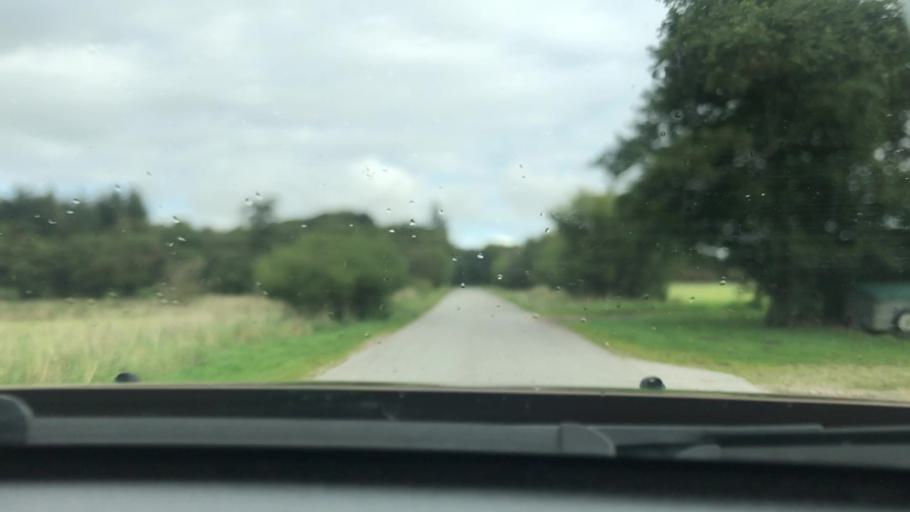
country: DK
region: South Denmark
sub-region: Esbjerg Kommune
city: Ribe
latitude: 55.2981
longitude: 8.7312
